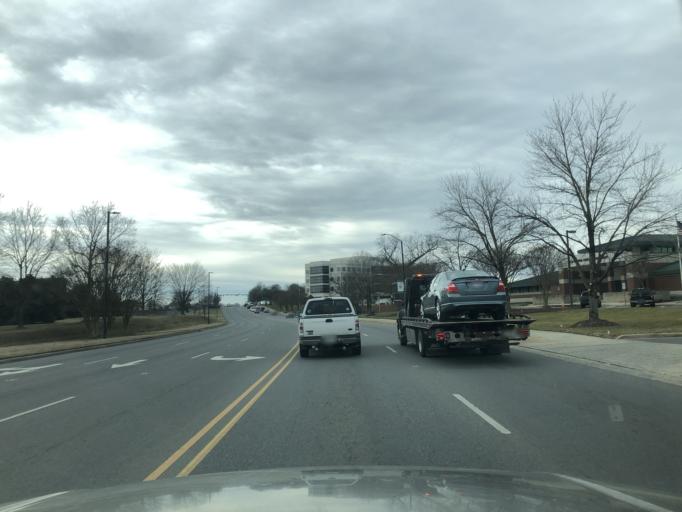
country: US
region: North Carolina
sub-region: Gaston County
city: Gastonia
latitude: 35.2658
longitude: -81.1783
